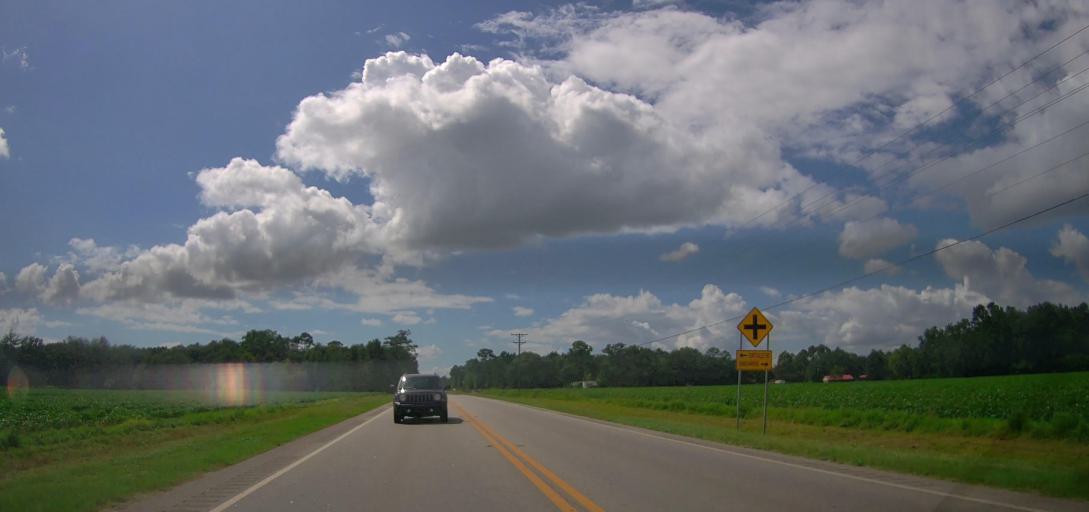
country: US
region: Georgia
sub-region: Coffee County
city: Broxton
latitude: 31.5539
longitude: -82.9616
